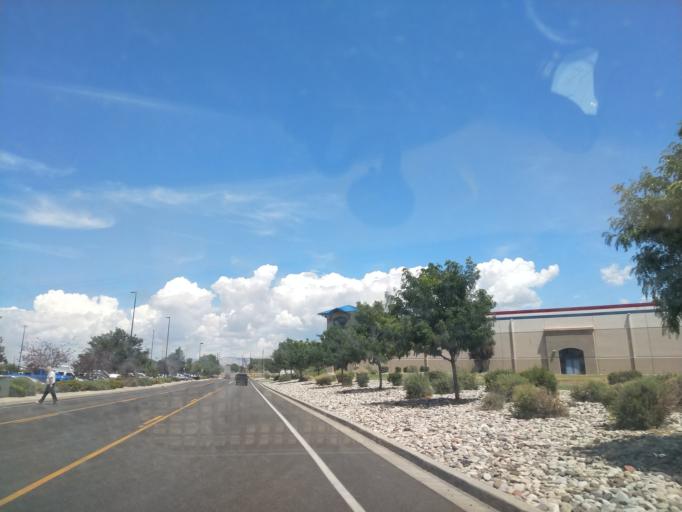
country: US
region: Colorado
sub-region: Mesa County
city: Grand Junction
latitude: 39.0755
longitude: -108.5801
